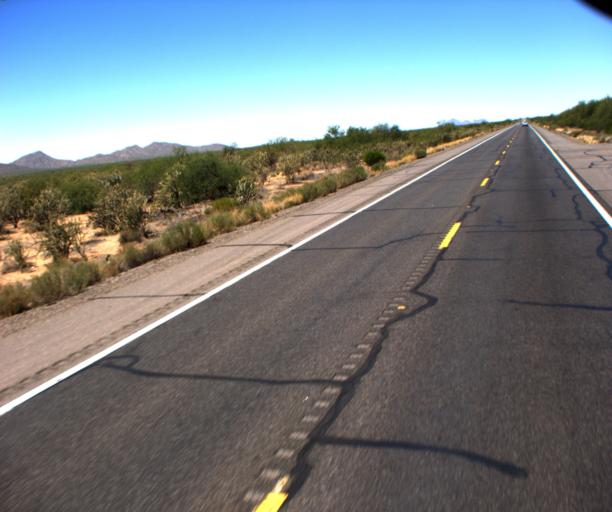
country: US
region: Arizona
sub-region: Yavapai County
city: Congress
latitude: 34.1090
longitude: -112.9298
